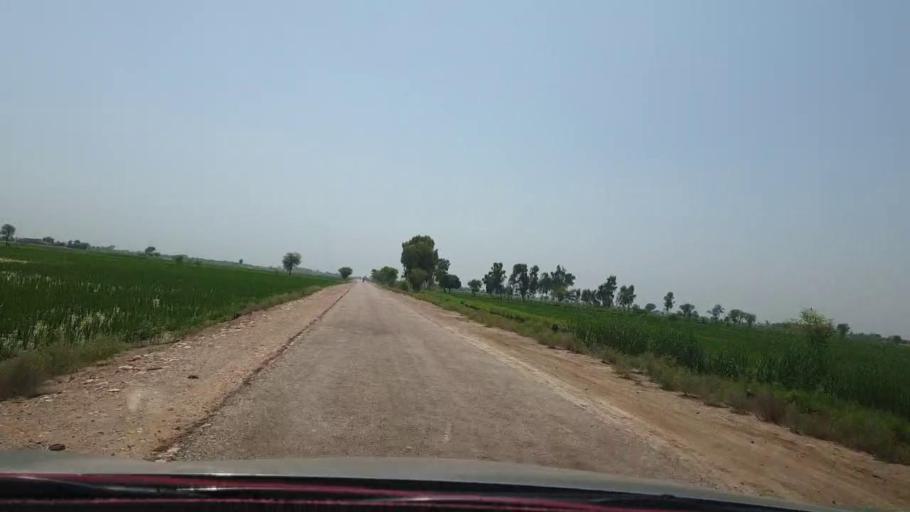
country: PK
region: Sindh
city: Warah
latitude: 27.5608
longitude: 67.8002
